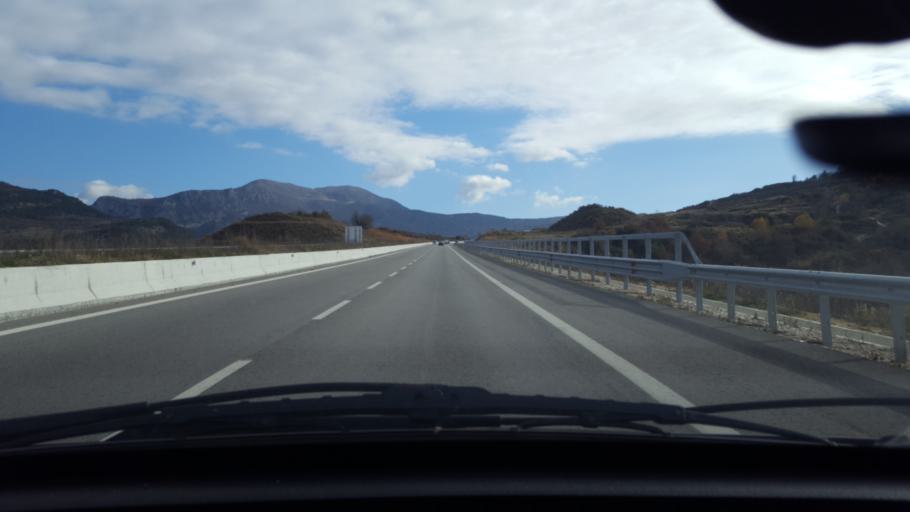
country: AL
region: Tirane
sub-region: Rrethi i Tiranes
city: Krrabe
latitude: 41.2259
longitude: 19.9372
